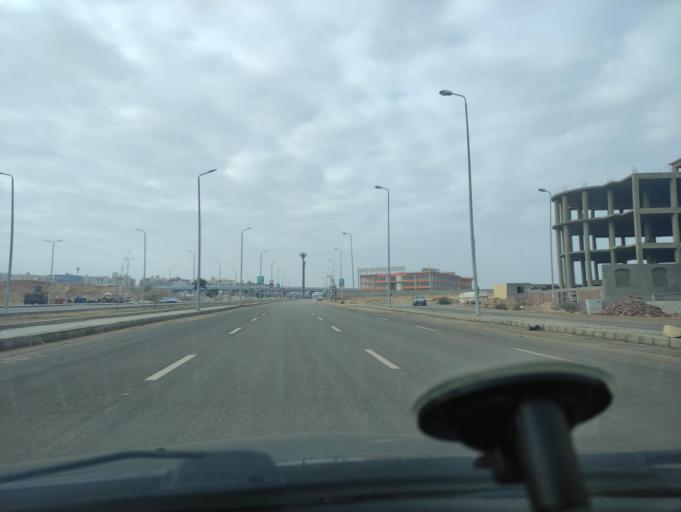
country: EG
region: Muhafazat al Qalyubiyah
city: Al Khankah
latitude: 30.0462
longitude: 31.5267
